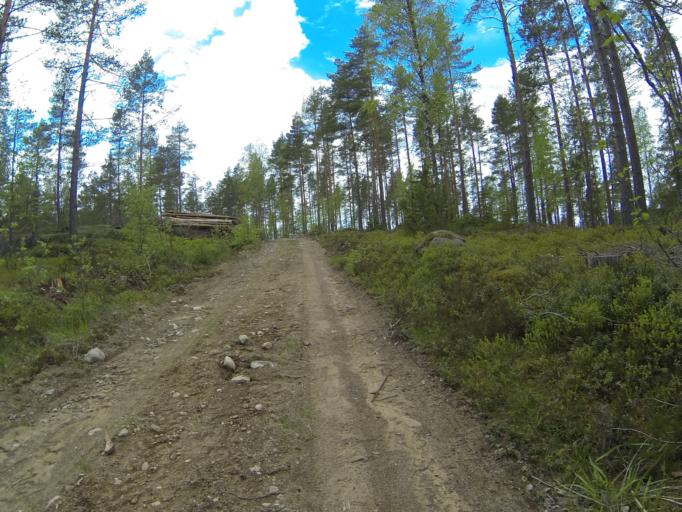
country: FI
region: Varsinais-Suomi
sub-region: Salo
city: Halikko
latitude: 60.3333
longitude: 23.0760
